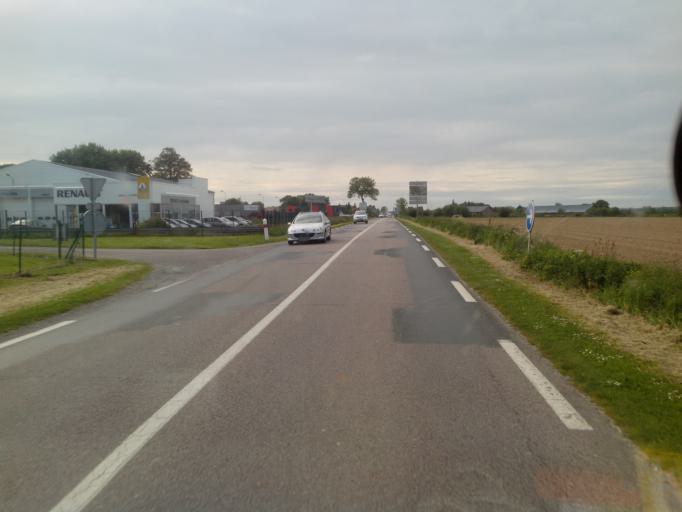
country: FR
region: Haute-Normandie
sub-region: Departement de la Seine-Maritime
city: Fauville-en-Caux
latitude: 49.6555
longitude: 0.5984
